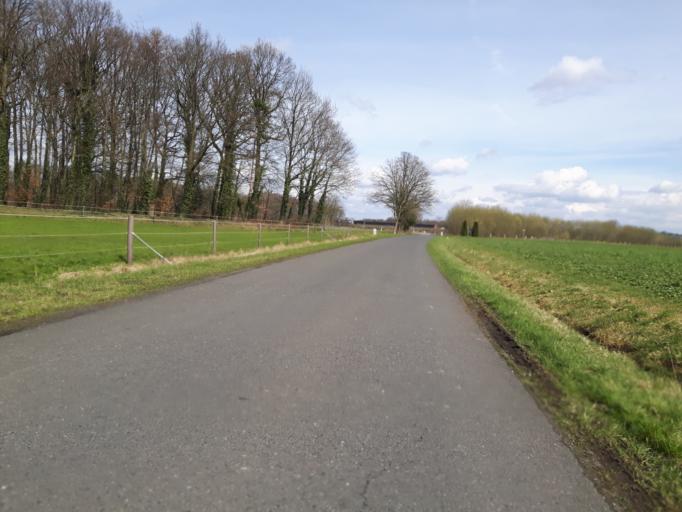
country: DE
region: North Rhine-Westphalia
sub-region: Regierungsbezirk Munster
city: Muenster
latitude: 51.9238
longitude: 7.5494
